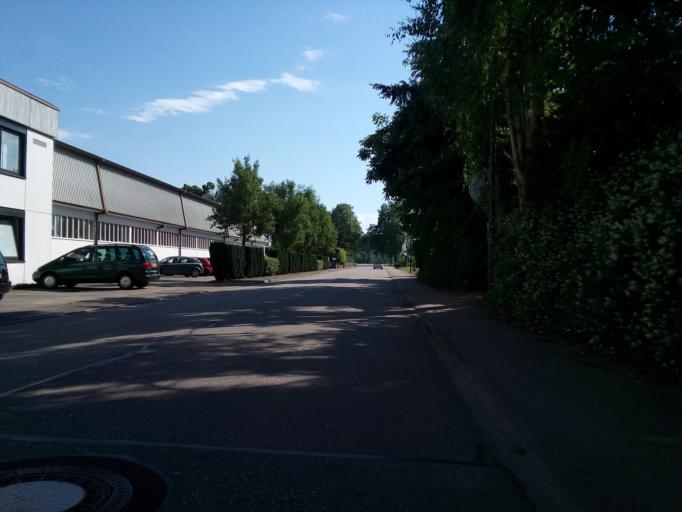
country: DE
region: Baden-Wuerttemberg
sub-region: Karlsruhe Region
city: Lichtenau
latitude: 48.7097
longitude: 7.9934
